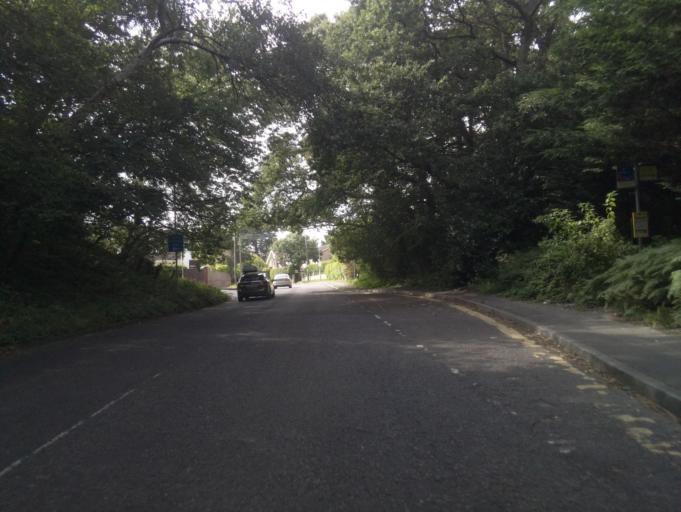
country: GB
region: England
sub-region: Hampshire
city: New Milton
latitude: 50.7513
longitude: -1.6836
